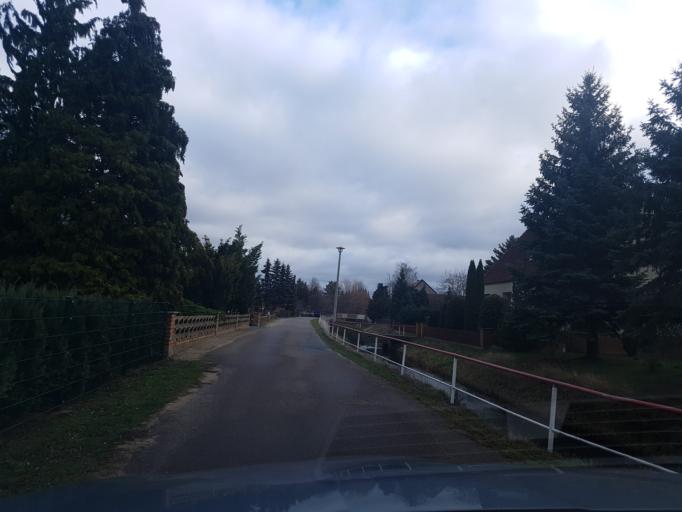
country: DE
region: Brandenburg
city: Falkenberg
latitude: 51.6351
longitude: 13.2370
